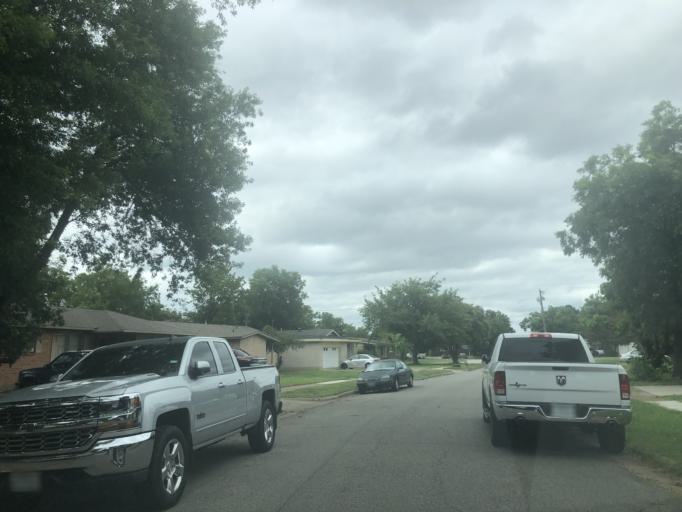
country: US
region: Texas
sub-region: Dallas County
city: Duncanville
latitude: 32.6558
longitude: -96.9102
